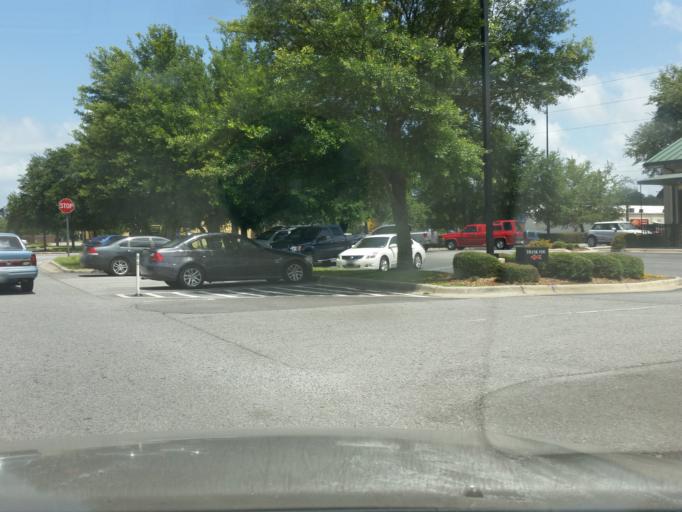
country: US
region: Florida
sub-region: Escambia County
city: Ferry Pass
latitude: 30.4959
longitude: -87.1938
